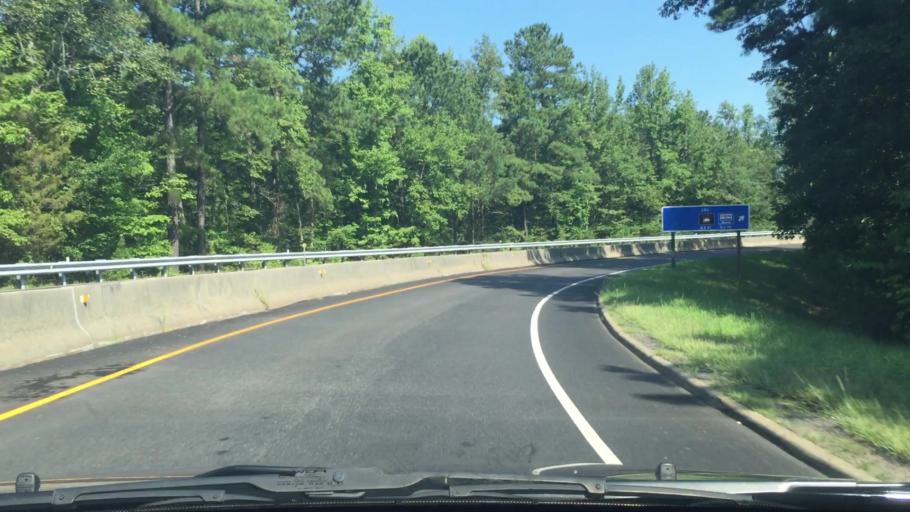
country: US
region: Virginia
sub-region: City of Petersburg
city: Petersburg
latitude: 37.0810
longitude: -77.3607
